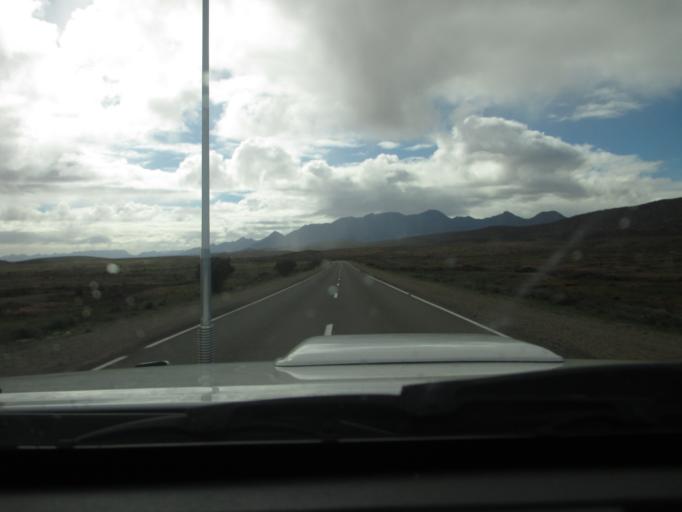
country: AU
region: South Australia
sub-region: Flinders Ranges
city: Quorn
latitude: -31.5946
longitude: 138.4091
